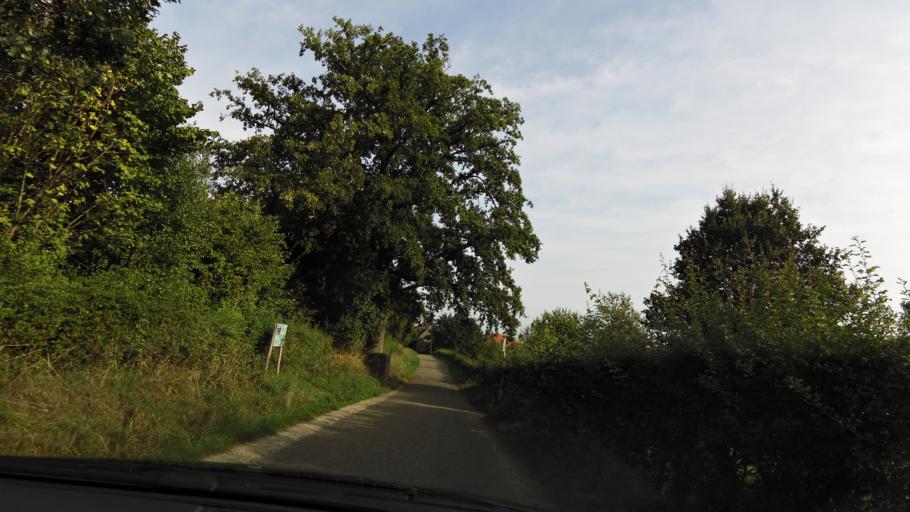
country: BE
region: Wallonia
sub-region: Province de Liege
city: Plombieres
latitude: 50.7651
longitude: 5.9227
